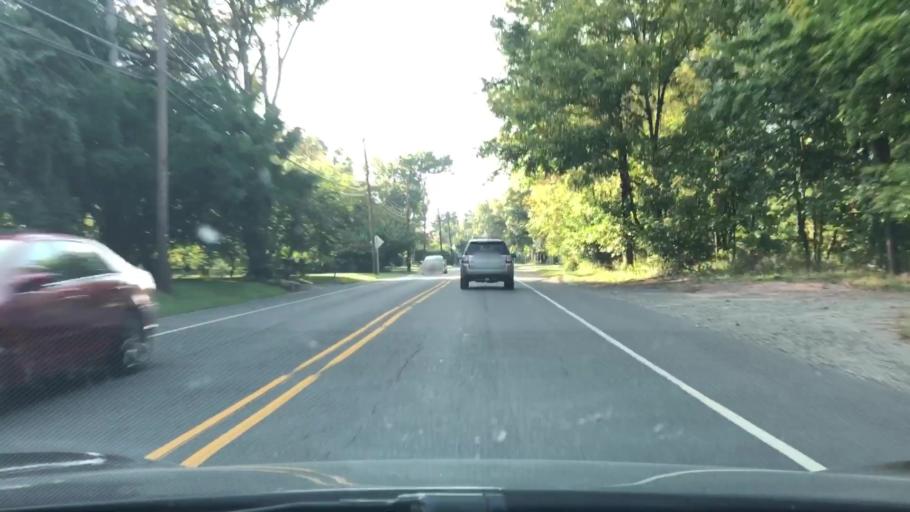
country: US
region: New Jersey
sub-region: Mercer County
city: Pennington
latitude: 40.3153
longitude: -74.7877
